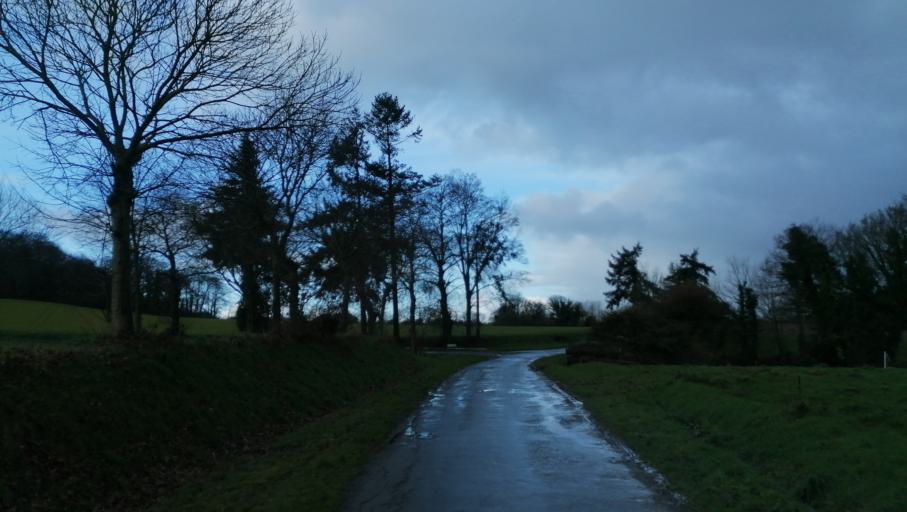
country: FR
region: Brittany
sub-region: Departement des Cotes-d'Armor
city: Plouagat
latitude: 48.4984
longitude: -2.9704
